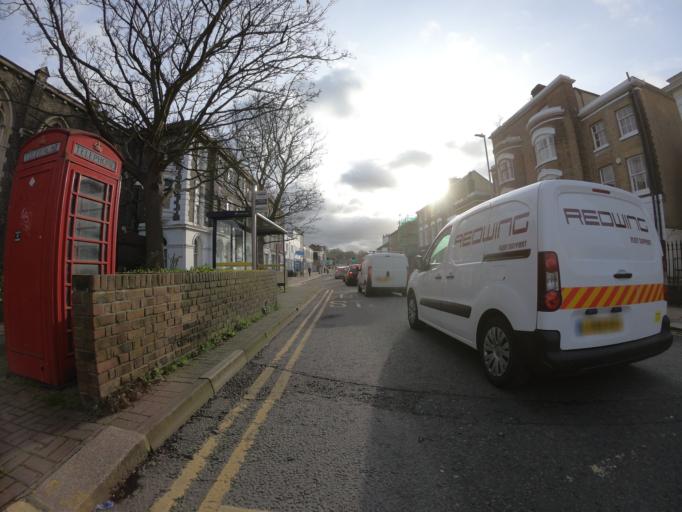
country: GB
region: England
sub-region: Kent
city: Gravesend
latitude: 51.4417
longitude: 0.3710
